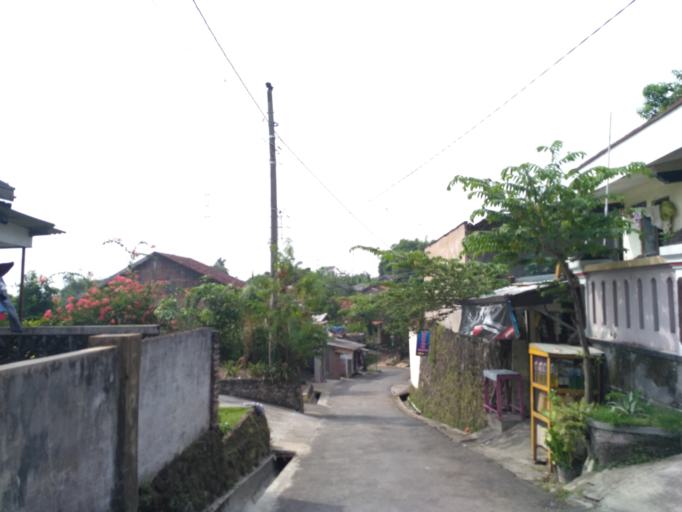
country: ID
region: Central Java
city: Semarang
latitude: -7.0244
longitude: 110.4429
